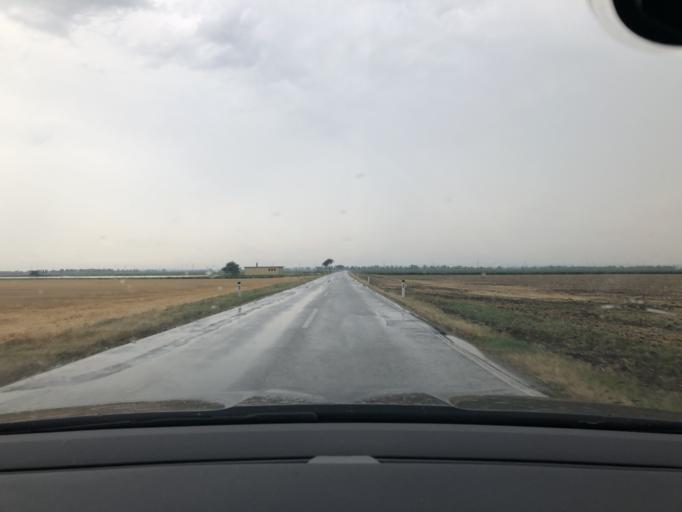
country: AT
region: Lower Austria
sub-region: Politischer Bezirk Ganserndorf
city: Weikendorf
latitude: 48.3116
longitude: 16.8217
